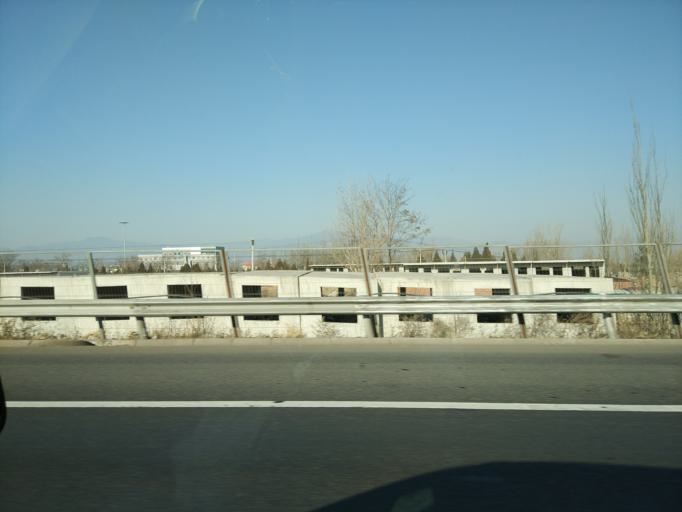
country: CN
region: Beijing
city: Kangzhuang
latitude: 40.3600
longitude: 115.9293
